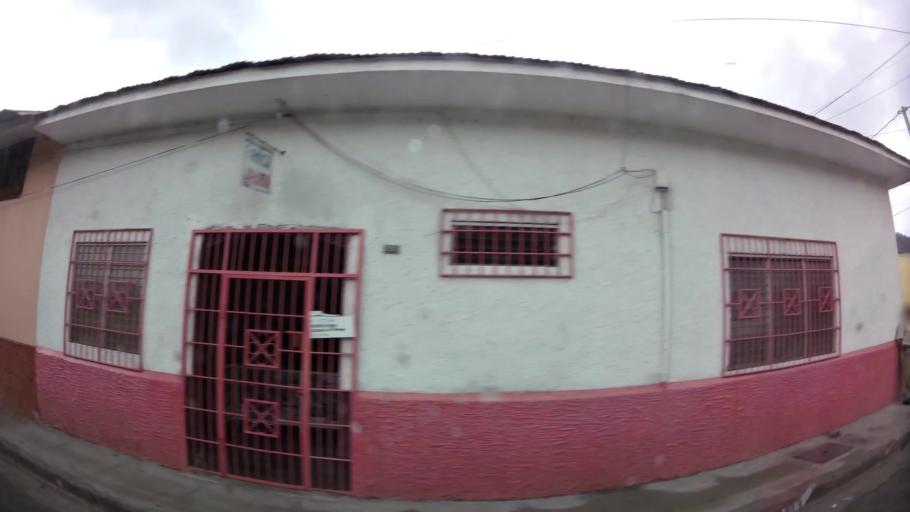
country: NI
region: Jinotega
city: Jinotega
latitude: 13.0933
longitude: -86.0037
